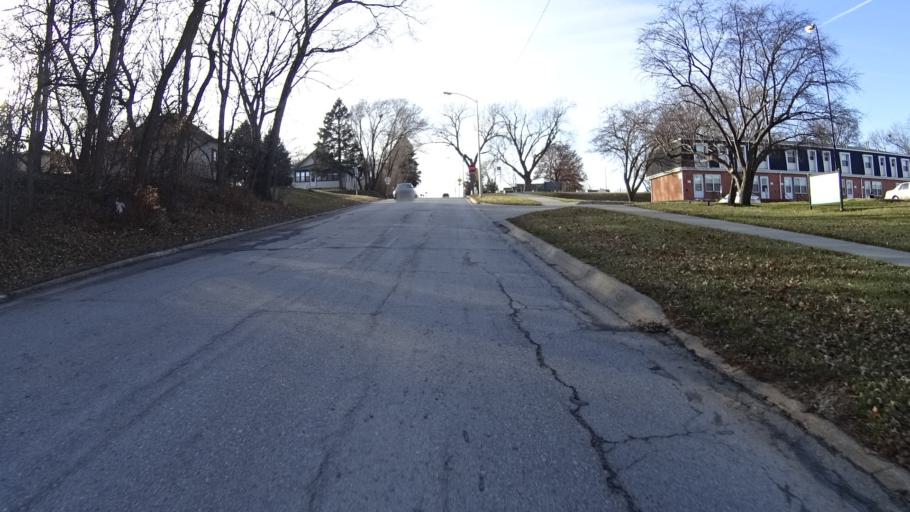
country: US
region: Nebraska
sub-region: Douglas County
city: Omaha
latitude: 41.1909
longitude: -95.9544
